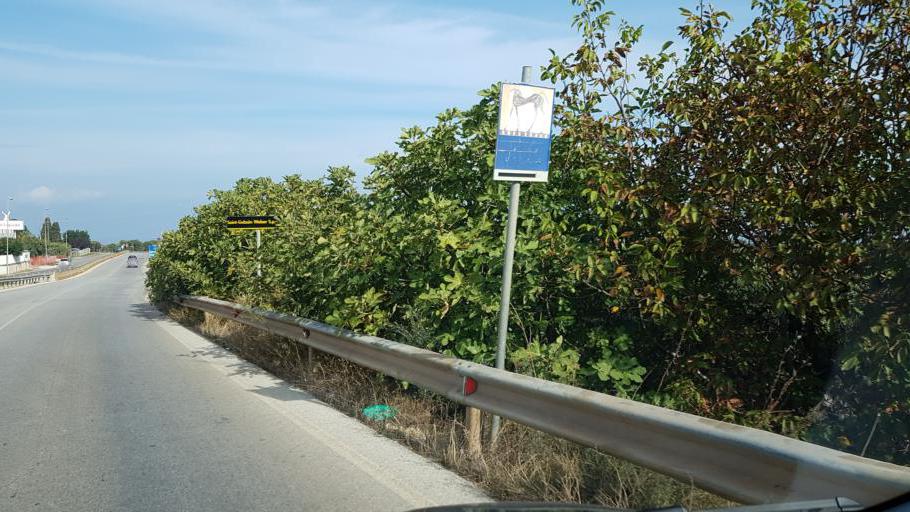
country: IT
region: Apulia
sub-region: Provincia di Brindisi
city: Ostuni
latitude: 40.7529
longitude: 17.5829
